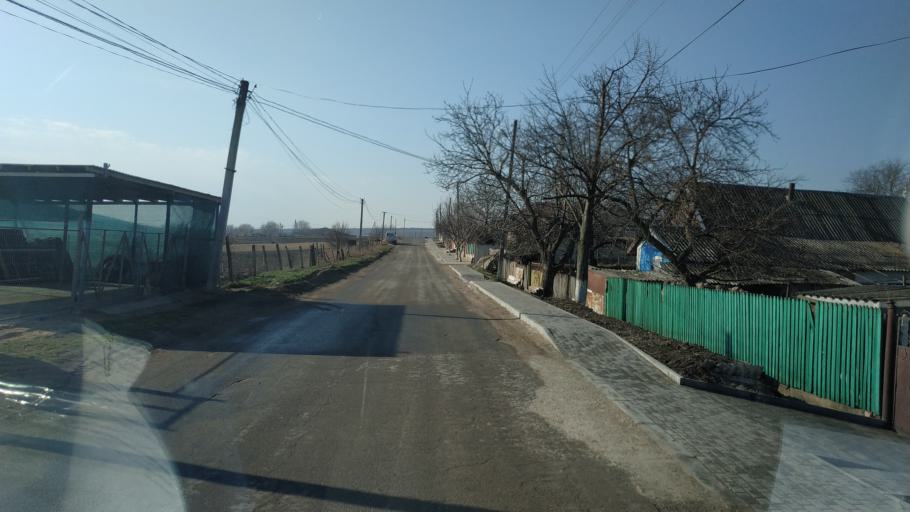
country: MD
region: Chisinau
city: Singera
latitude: 46.8077
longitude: 29.0347
